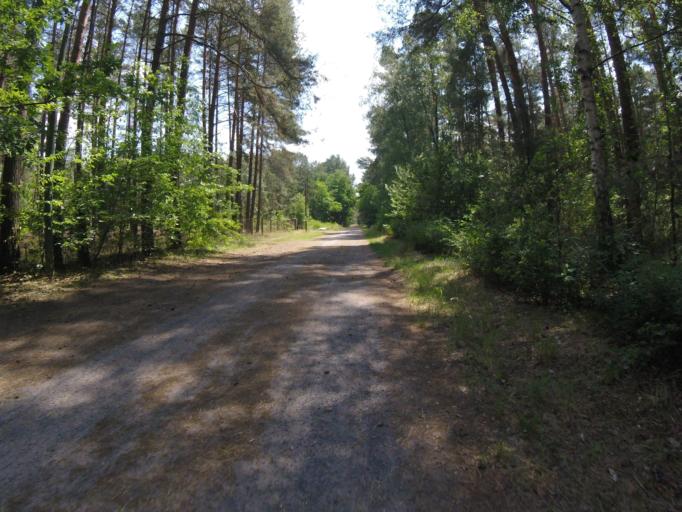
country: DE
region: Brandenburg
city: Bestensee
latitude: 52.2483
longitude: 13.7305
